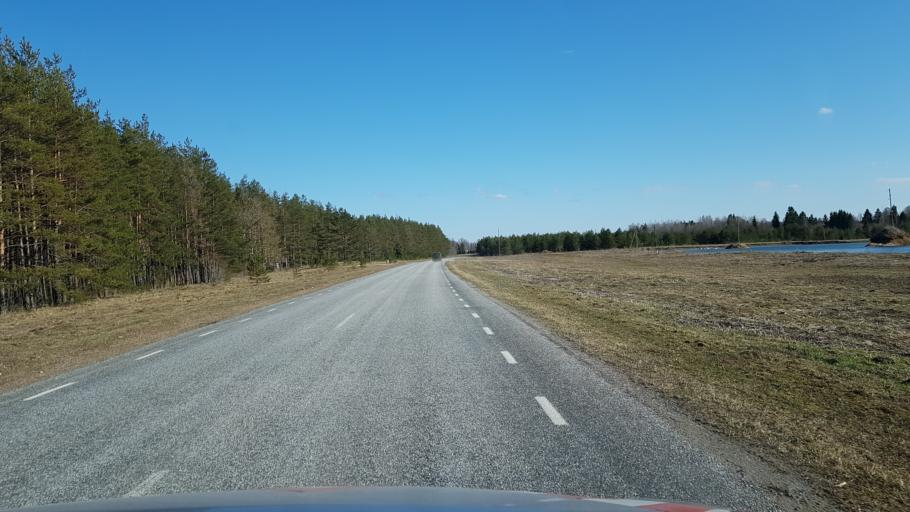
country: EE
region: Laeaene-Virumaa
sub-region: Haljala vald
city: Haljala
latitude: 59.4692
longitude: 26.1774
